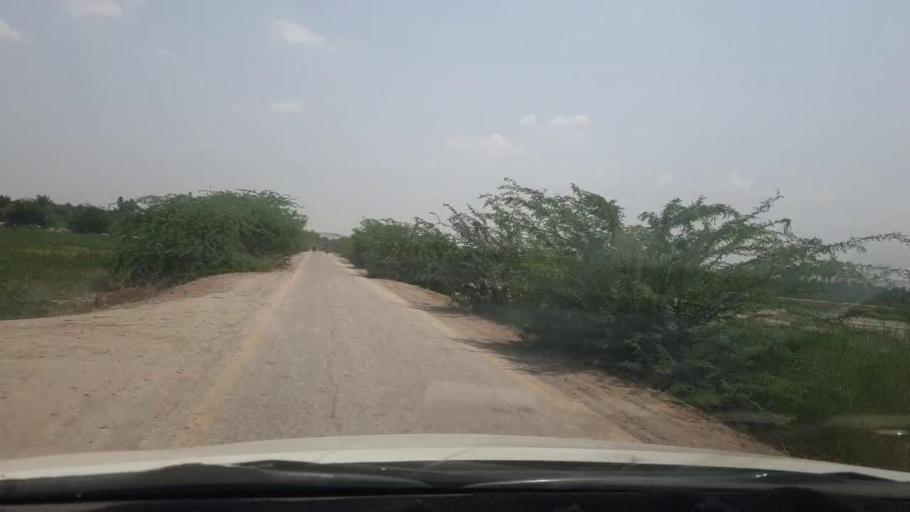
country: PK
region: Sindh
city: Khairpur
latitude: 27.5348
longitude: 68.8889
